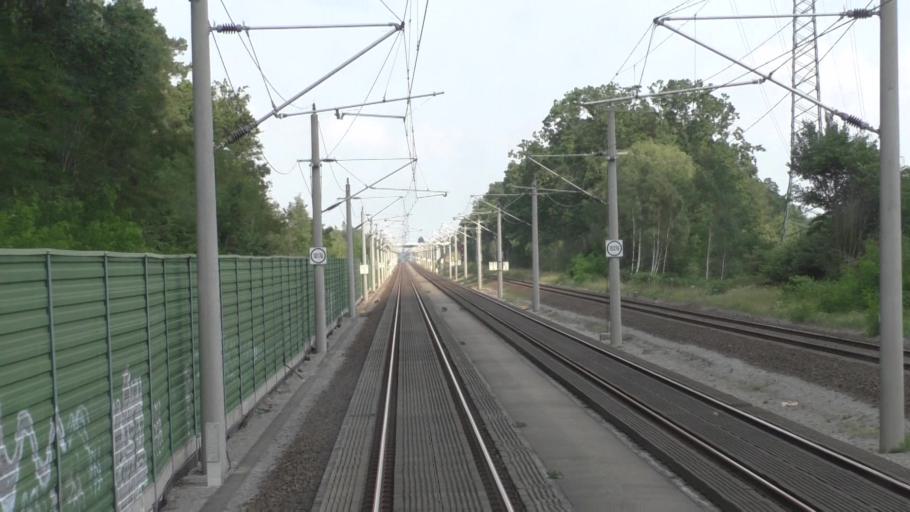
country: DE
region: Saxony-Anhalt
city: Schollene
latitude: 52.5905
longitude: 12.2017
